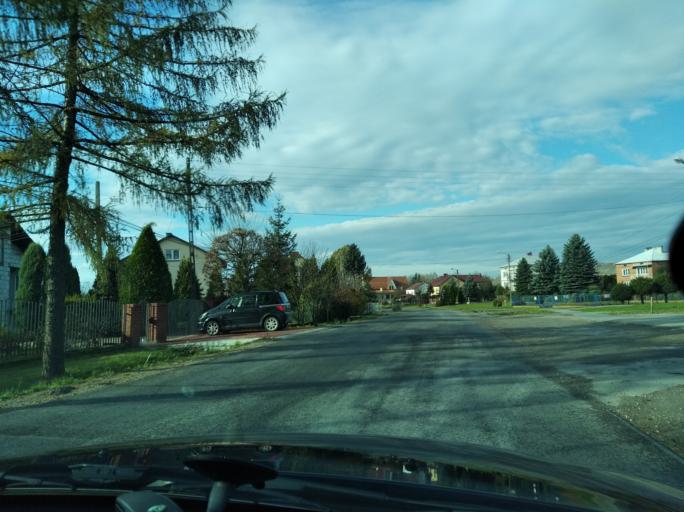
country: PL
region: Subcarpathian Voivodeship
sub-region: Powiat ropczycko-sedziszowski
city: Sedziszow Malopolski
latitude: 50.0783
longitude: 21.7404
